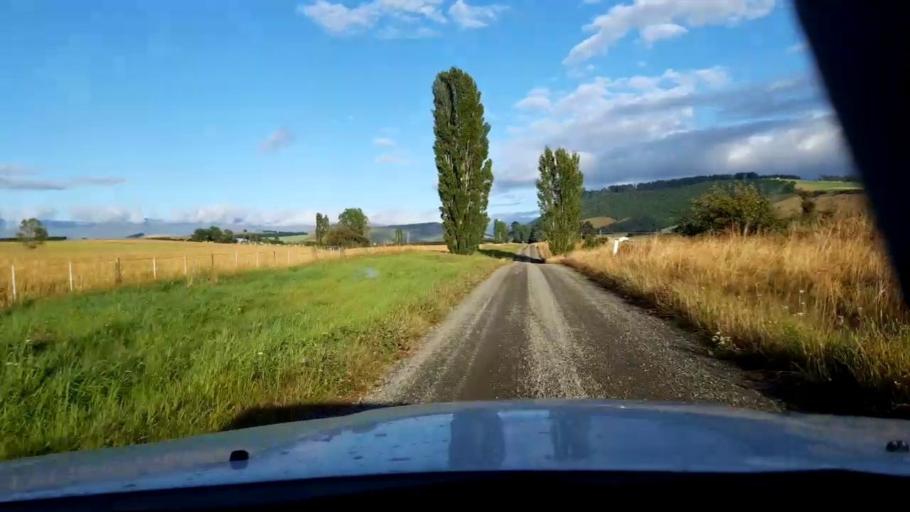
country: NZ
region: Canterbury
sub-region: Timaru District
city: Timaru
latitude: -44.4251
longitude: 171.1121
